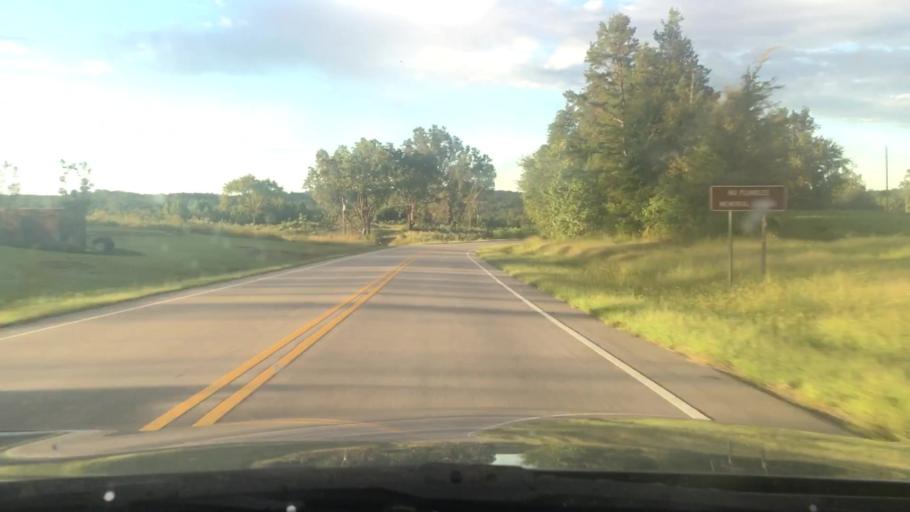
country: US
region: North Carolina
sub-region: Caswell County
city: Yanceyville
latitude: 36.3958
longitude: -79.3298
